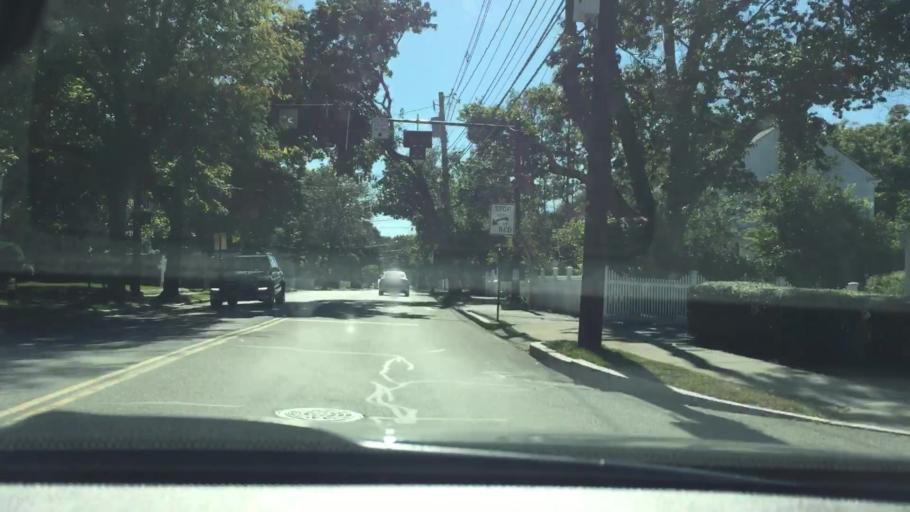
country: US
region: Massachusetts
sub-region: Middlesex County
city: Newton
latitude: 42.3146
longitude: -71.1955
